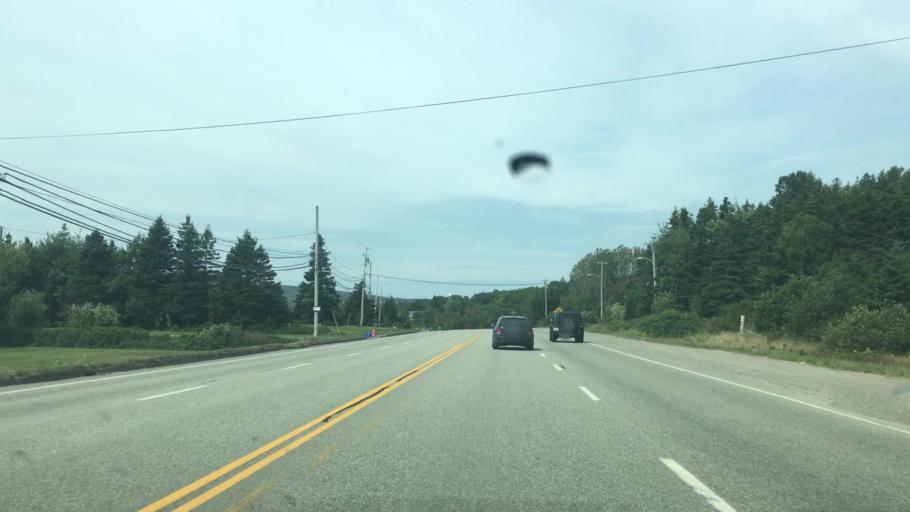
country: CA
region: Nova Scotia
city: Port Hawkesbury
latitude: 45.6420
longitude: -61.3910
